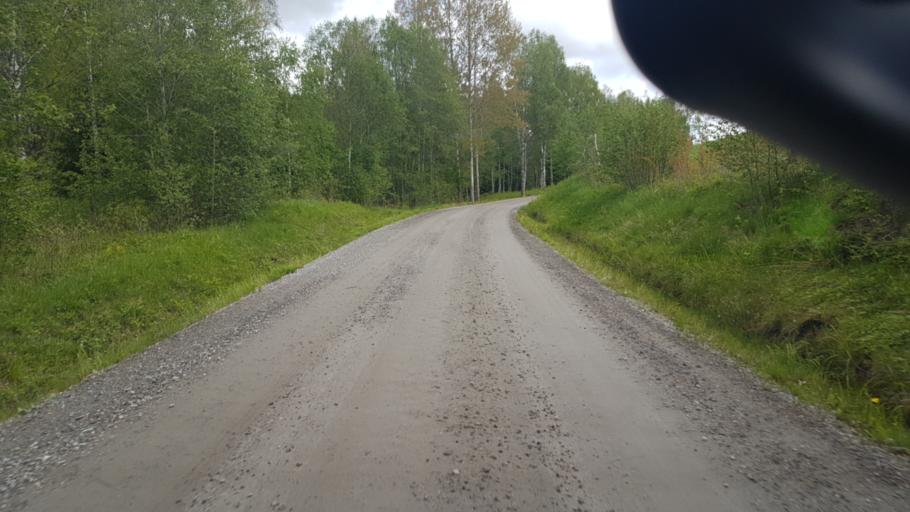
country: NO
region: Ostfold
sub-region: Romskog
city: Romskog
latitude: 59.6833
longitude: 11.9314
